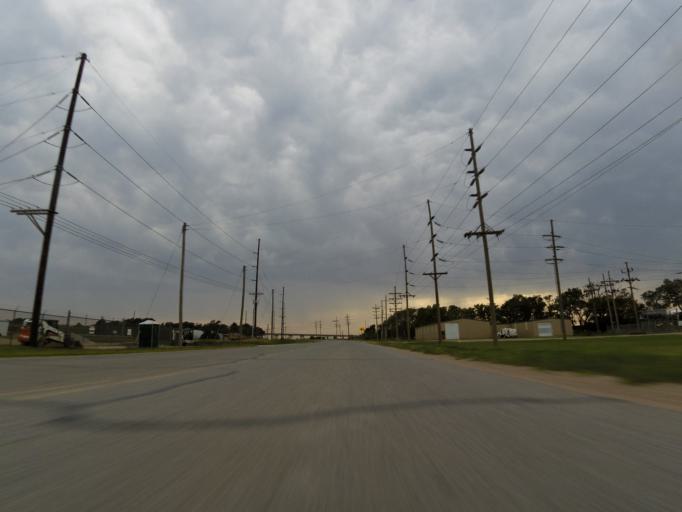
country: US
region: Kansas
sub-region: Reno County
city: South Hutchinson
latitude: 38.0281
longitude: -97.9735
